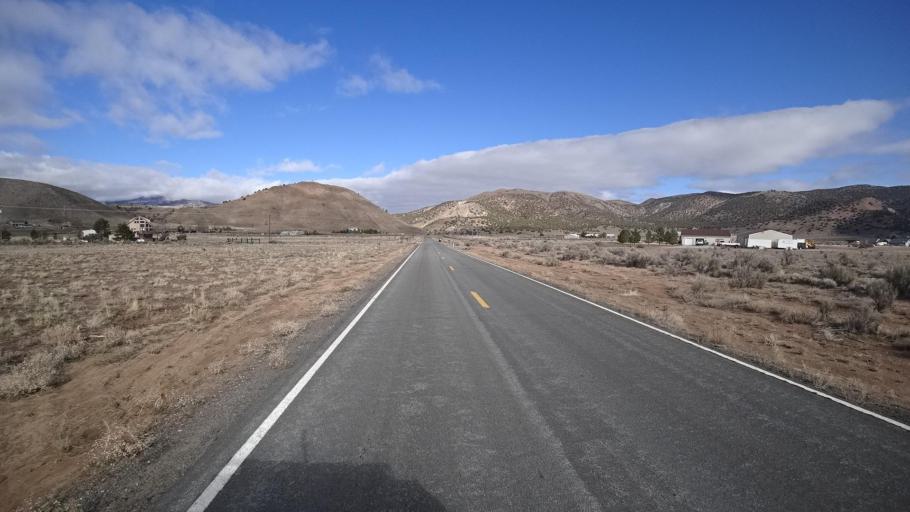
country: US
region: Nevada
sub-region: Washoe County
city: Cold Springs
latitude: 39.8942
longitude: -119.9798
